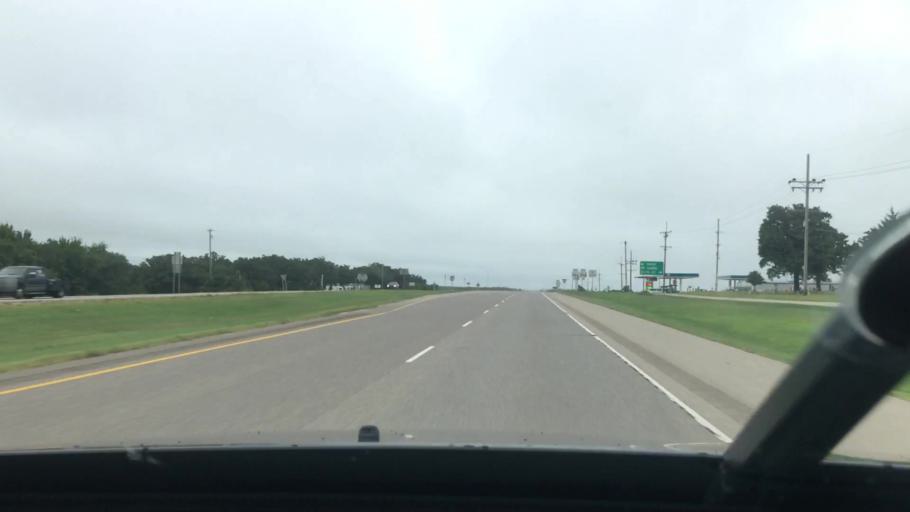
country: US
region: Oklahoma
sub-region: Seminole County
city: Seminole
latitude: 35.3465
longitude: -96.6715
